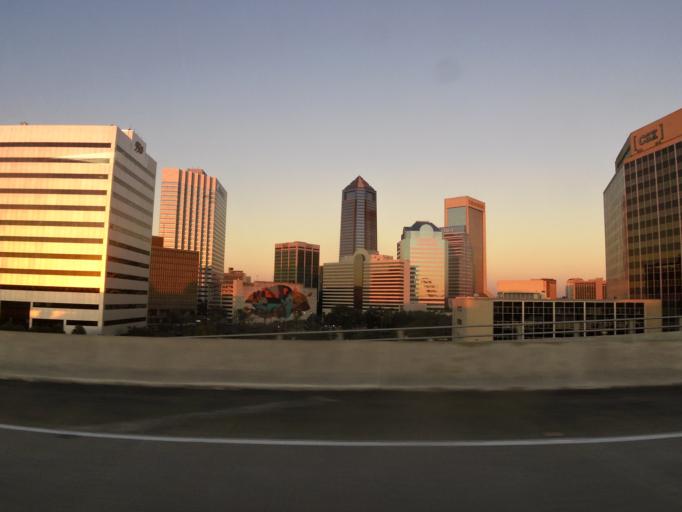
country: US
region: Florida
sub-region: Duval County
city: Jacksonville
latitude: 30.3246
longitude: -81.6658
